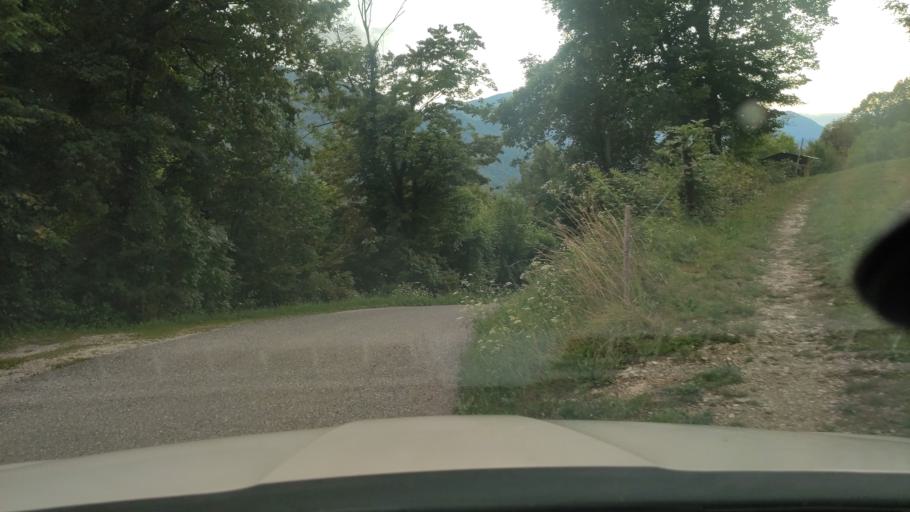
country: IT
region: Friuli Venezia Giulia
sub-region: Provincia di Udine
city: Cras
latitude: 46.2149
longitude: 13.6464
